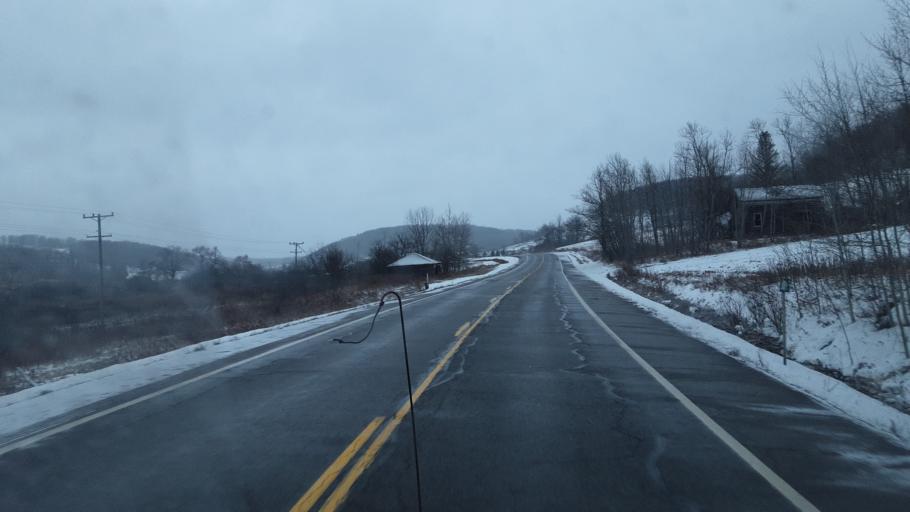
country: US
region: Pennsylvania
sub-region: Tioga County
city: Westfield
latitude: 42.0714
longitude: -77.5482
